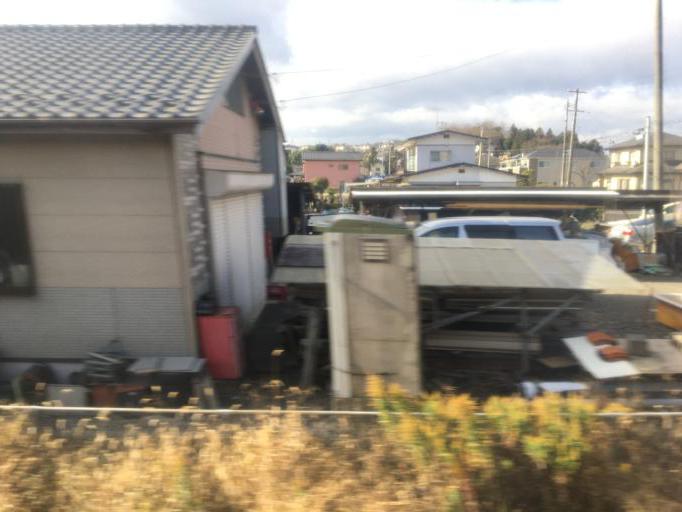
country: JP
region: Miyagi
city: Iwanuma
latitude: 38.1561
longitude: 140.8862
